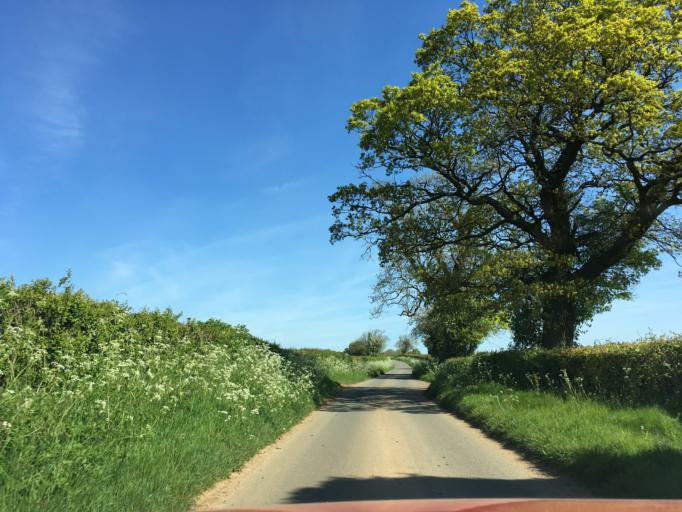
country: GB
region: England
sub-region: Wiltshire
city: Luckington
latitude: 51.5964
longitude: -2.2559
